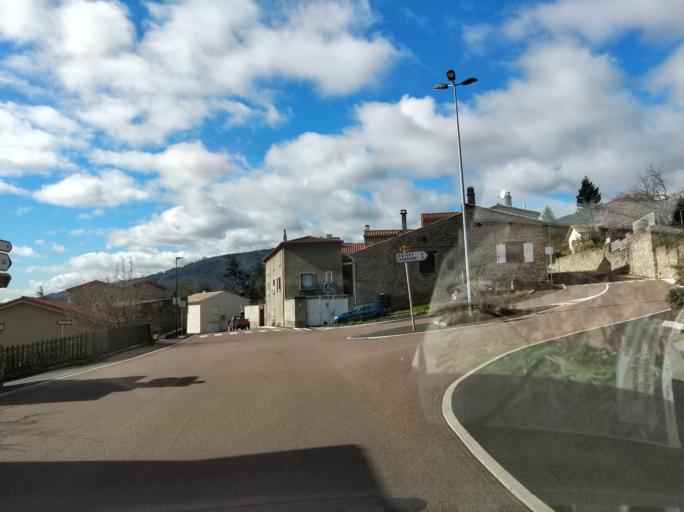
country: FR
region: Rhone-Alpes
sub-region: Departement de la Loire
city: Pelussin
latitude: 45.3994
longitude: 4.6867
